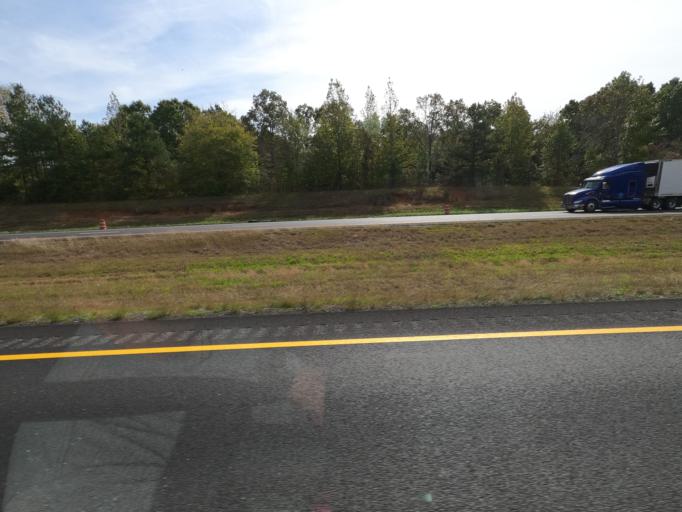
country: US
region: Tennessee
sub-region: Decatur County
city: Parsons
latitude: 35.8313
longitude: -88.1033
